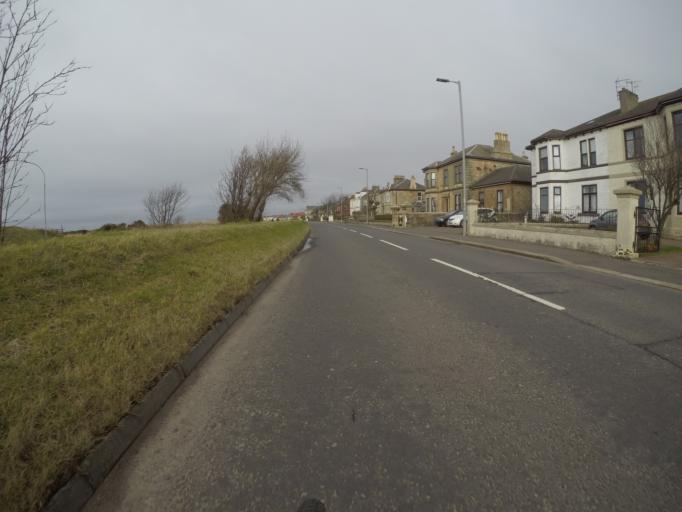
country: GB
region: Scotland
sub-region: North Ayrshire
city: Ardrossan
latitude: 55.6478
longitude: -4.8134
